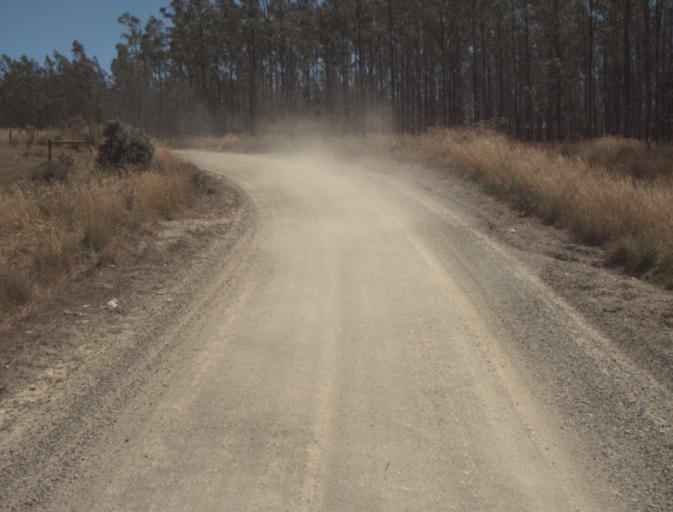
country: AU
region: Tasmania
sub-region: Dorset
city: Scottsdale
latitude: -41.3298
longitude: 147.4401
